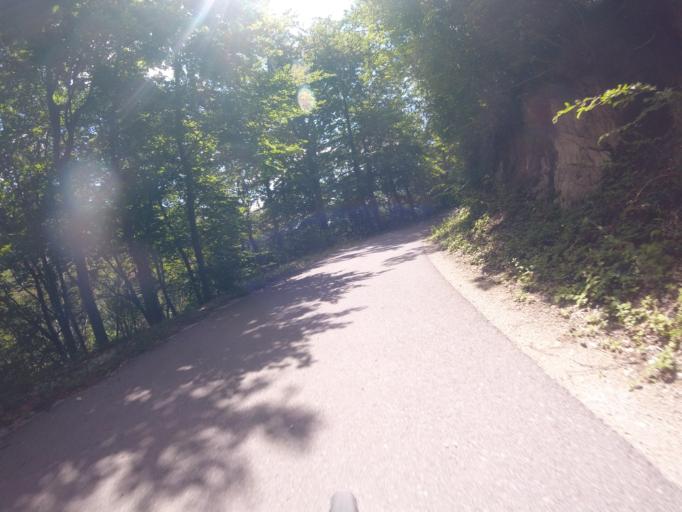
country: SI
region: Kostanjevica na Krki
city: Kostanjevica na Krki
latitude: 45.7673
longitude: 15.4117
